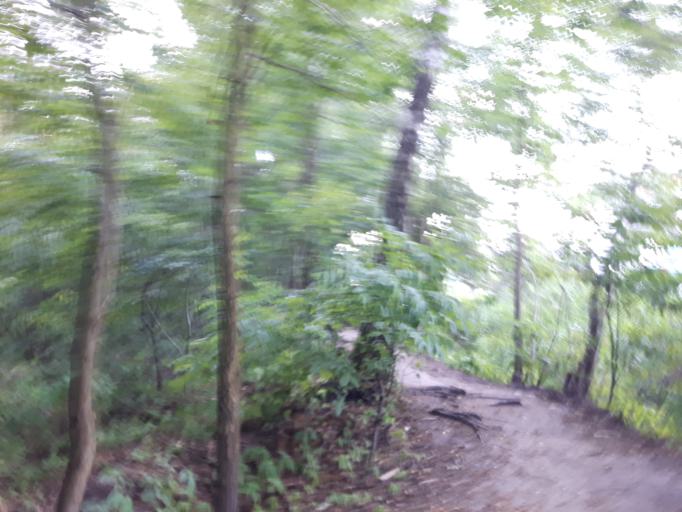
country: PL
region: Masovian Voivodeship
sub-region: Powiat wolominski
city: Zabki
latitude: 52.2775
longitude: 21.1341
